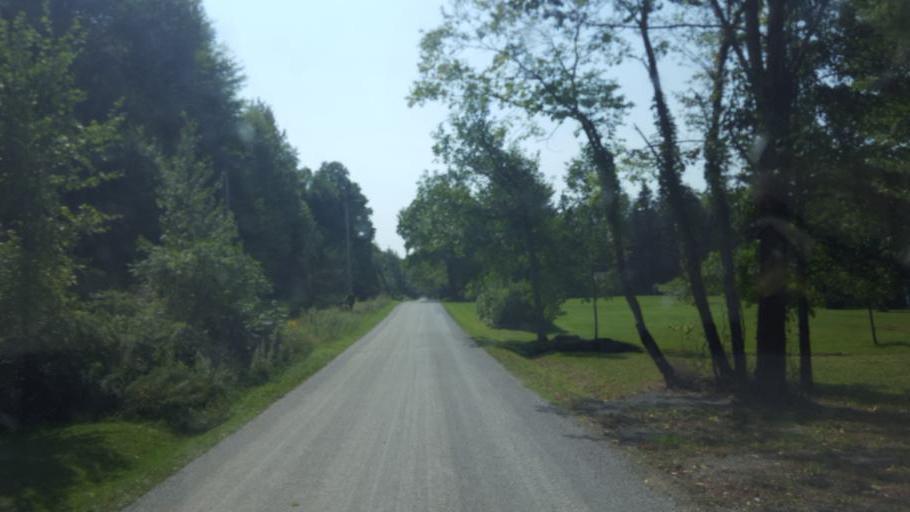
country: US
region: Ohio
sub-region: Ashtabula County
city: Orwell
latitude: 41.5240
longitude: -80.8846
